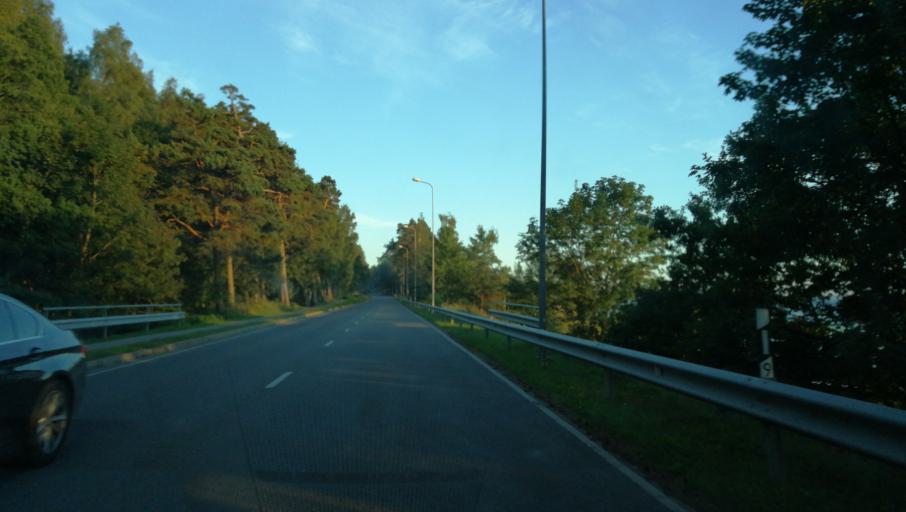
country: LV
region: Saulkrastu
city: Saulkrasti
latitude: 57.2883
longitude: 24.4126
